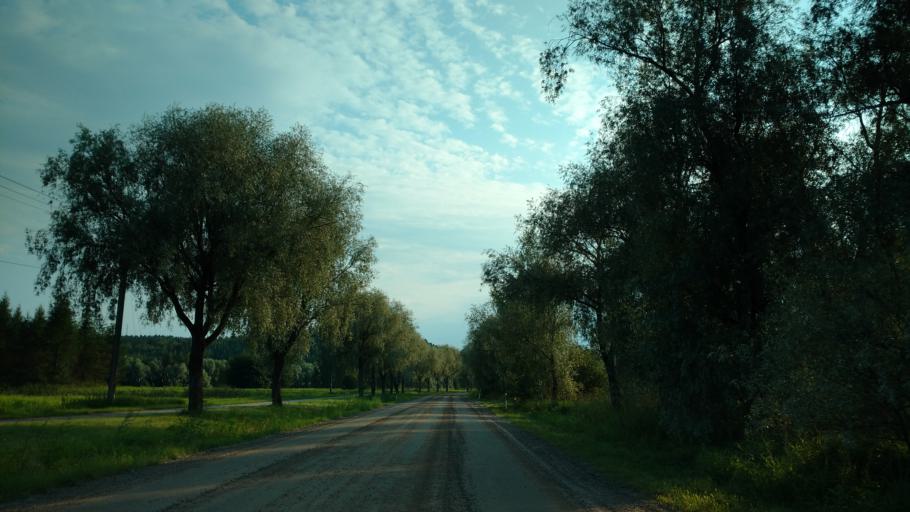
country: FI
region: Varsinais-Suomi
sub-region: Salo
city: Halikko
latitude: 60.3700
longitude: 23.1001
